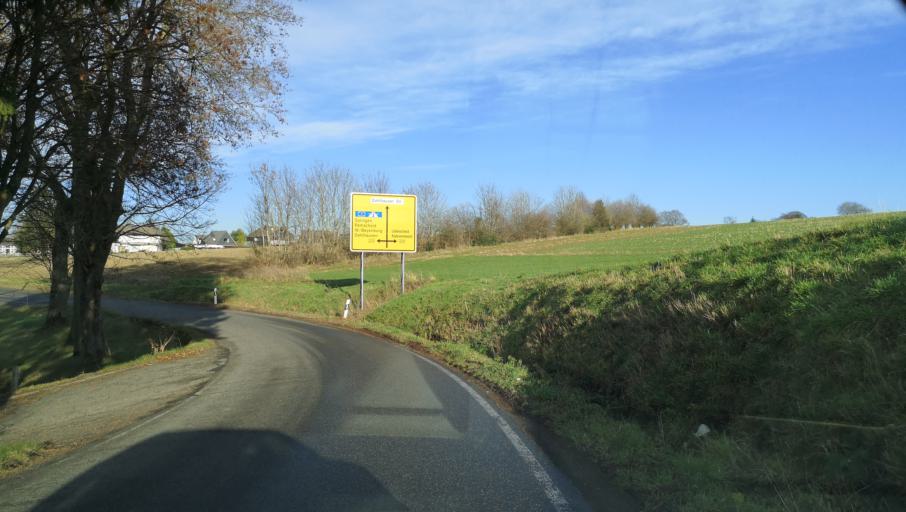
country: DE
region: North Rhine-Westphalia
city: Radevormwald
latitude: 51.1997
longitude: 7.3212
